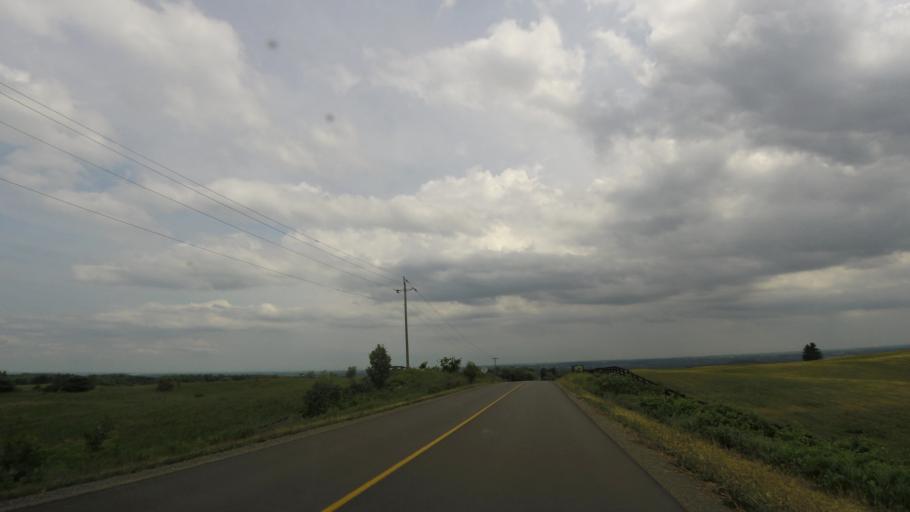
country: CA
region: Ontario
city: Orangeville
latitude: 43.8688
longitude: -79.9360
